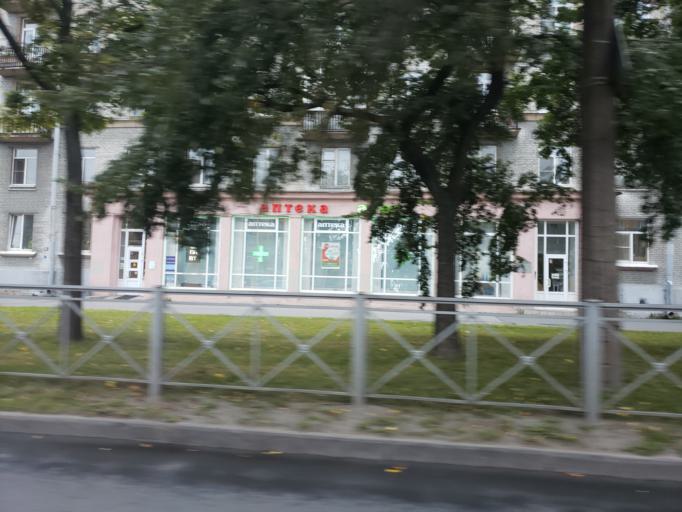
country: RU
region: St.-Petersburg
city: Vasyl'evsky Ostrov
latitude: 59.9375
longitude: 30.2333
